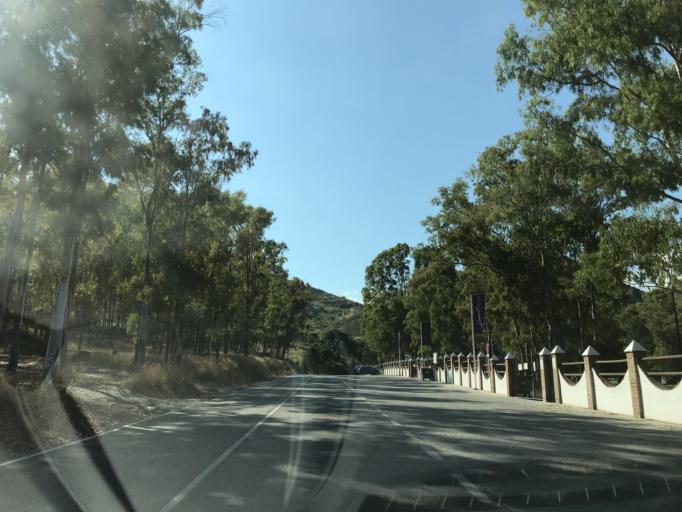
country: ES
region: Andalusia
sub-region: Provincia de Malaga
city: Benahavis
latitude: 36.5075
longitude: -5.0332
